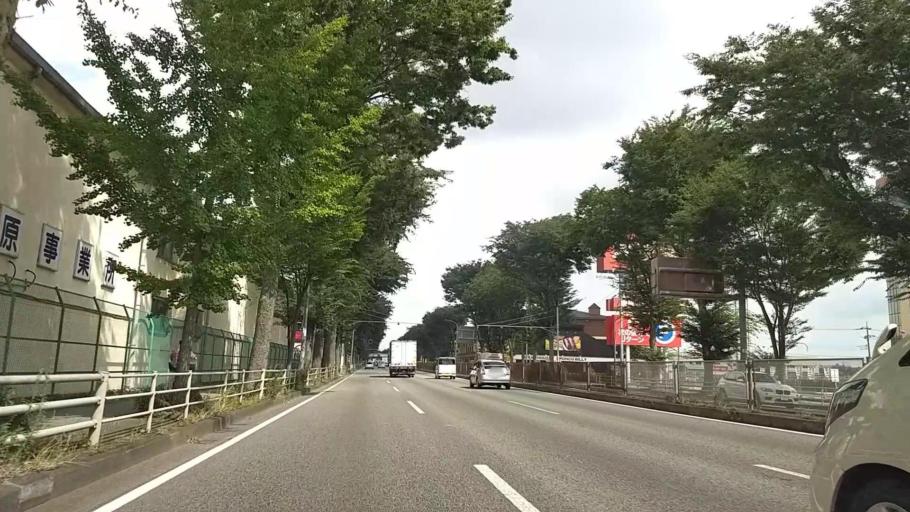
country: JP
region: Tokyo
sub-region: Machida-shi
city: Machida
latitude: 35.5195
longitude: 139.4529
